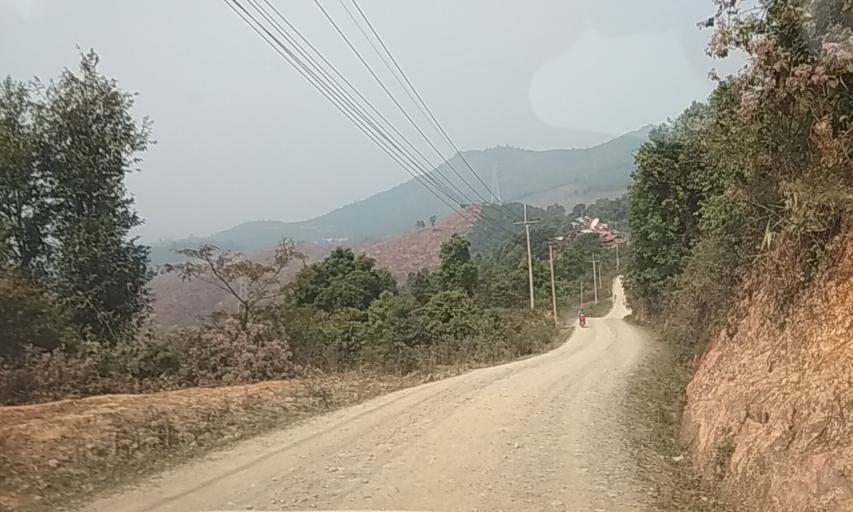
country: TH
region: Nan
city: Chaloem Phra Kiat
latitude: 20.0172
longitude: 101.1080
